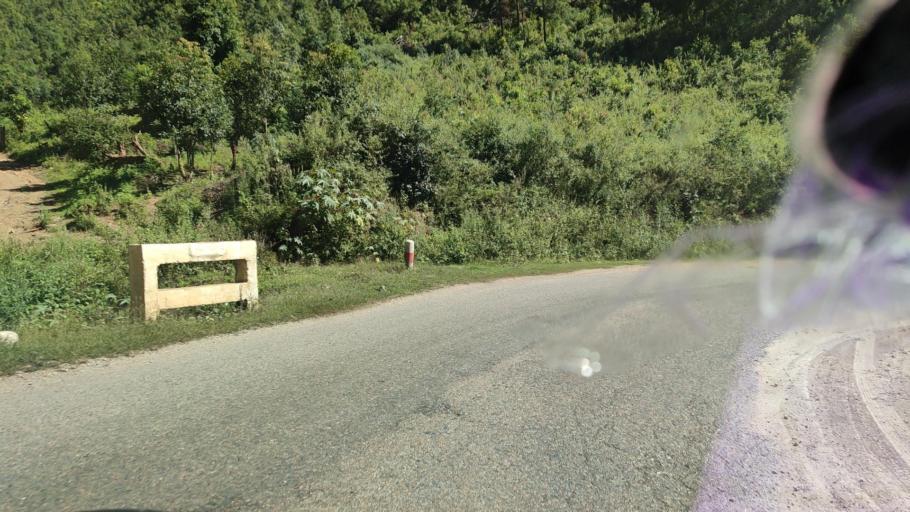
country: MM
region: Shan
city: Taunggyi
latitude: 20.8750
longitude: 97.4826
